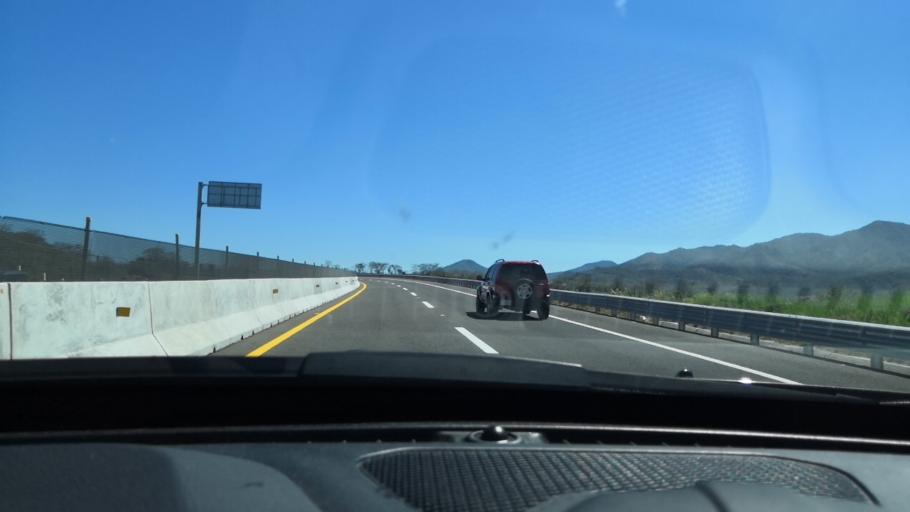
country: MX
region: Nayarit
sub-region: Compostela
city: Juan Escutia (Borbollon)
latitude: 21.1194
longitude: -104.8881
